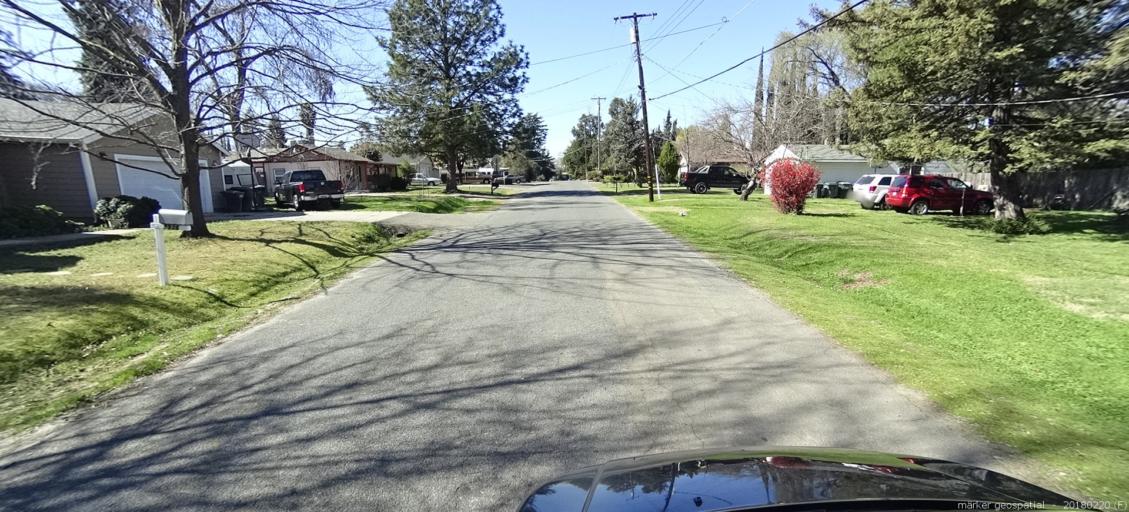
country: US
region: California
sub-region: Sacramento County
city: Orangevale
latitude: 38.6816
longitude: -121.2239
